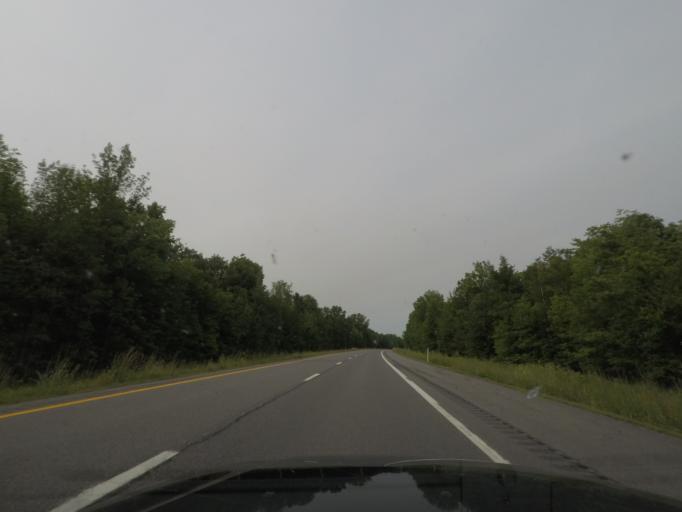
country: US
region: New York
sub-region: Clinton County
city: Champlain
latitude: 44.9003
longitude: -73.4543
